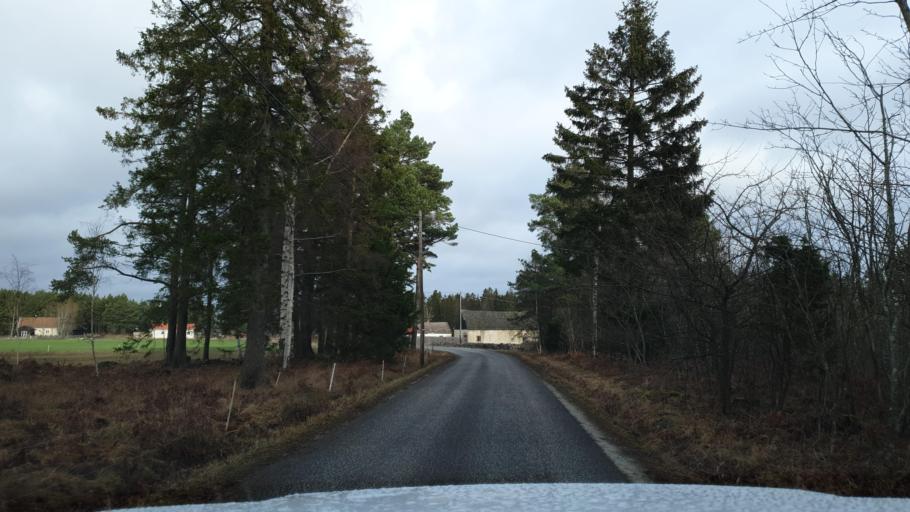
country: SE
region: Gotland
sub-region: Gotland
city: Slite
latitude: 57.3830
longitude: 18.8080
